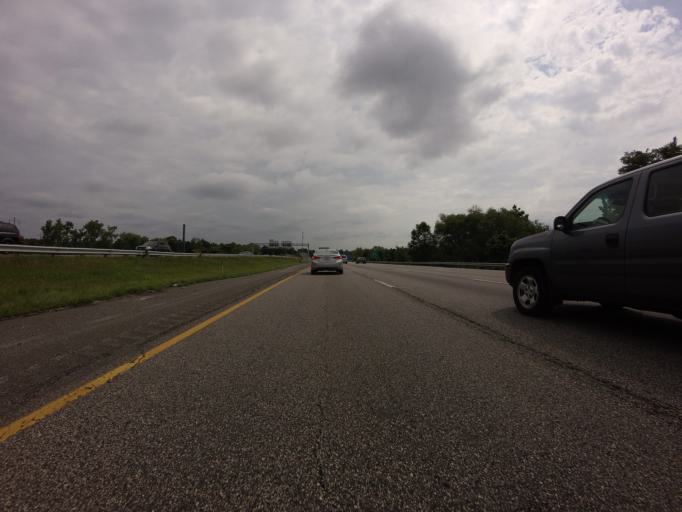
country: US
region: Pennsylvania
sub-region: Delaware County
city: Woodlyn
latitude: 39.8678
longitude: -75.3325
